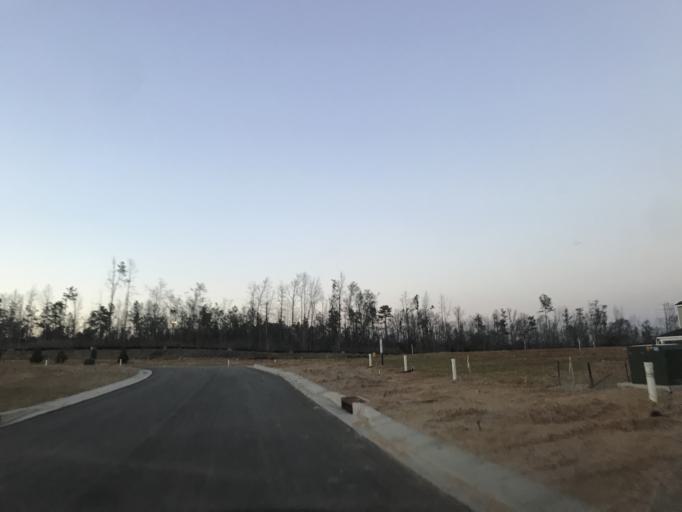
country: US
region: North Carolina
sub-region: Wake County
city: Raleigh
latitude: 35.8709
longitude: -78.5738
